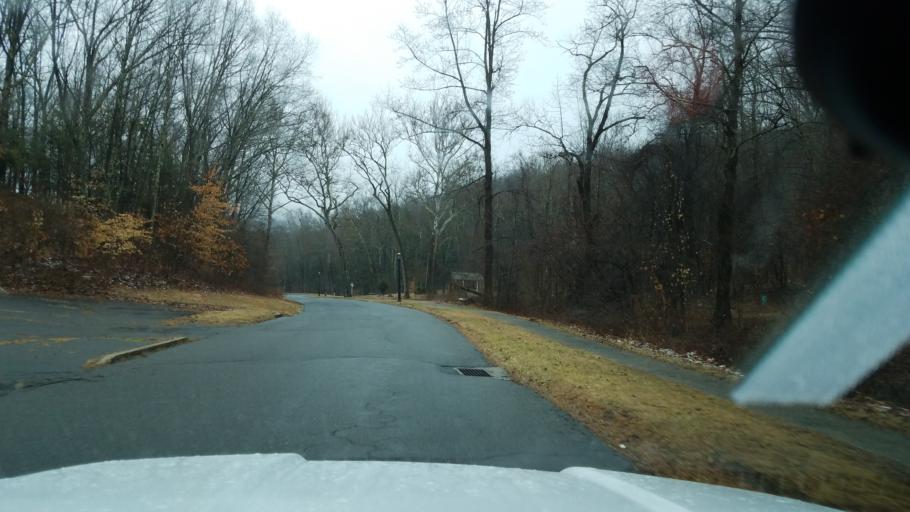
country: US
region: Connecticut
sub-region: New Haven County
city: Heritage Village
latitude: 41.4945
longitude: -73.2670
